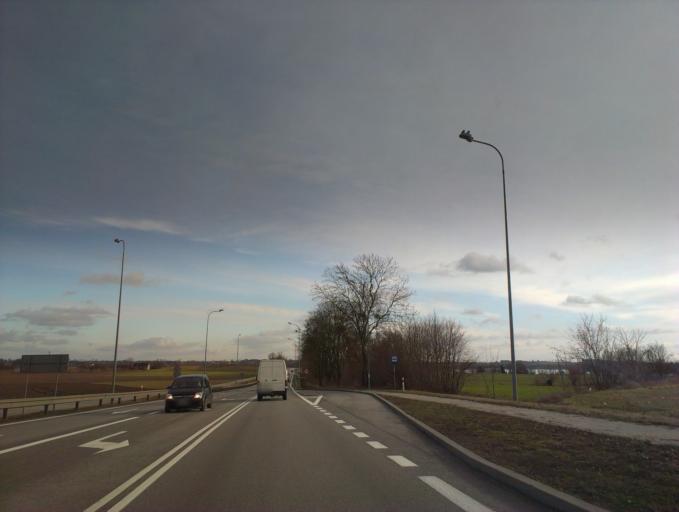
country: PL
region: Kujawsko-Pomorskie
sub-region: Powiat lipnowski
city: Kikol
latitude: 52.9263
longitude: 19.0841
